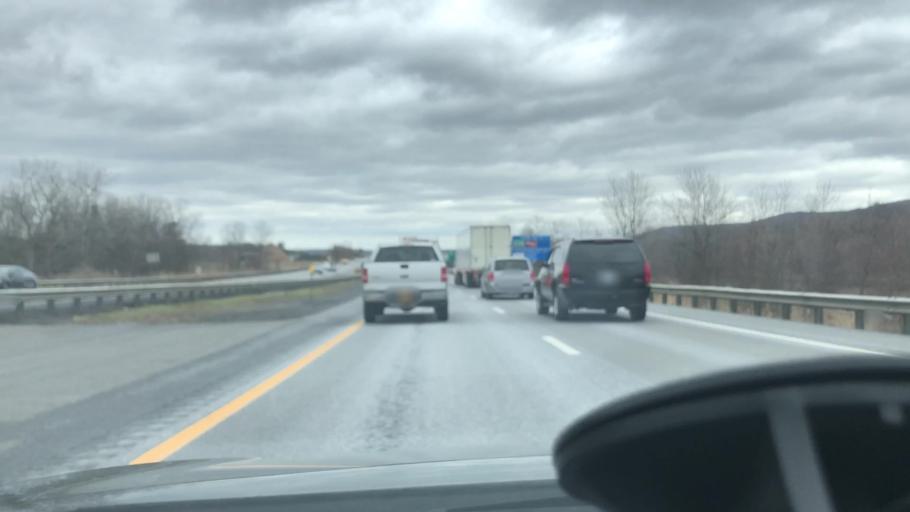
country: US
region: New York
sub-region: Herkimer County
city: Mohawk
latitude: 43.0172
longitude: -75.0042
